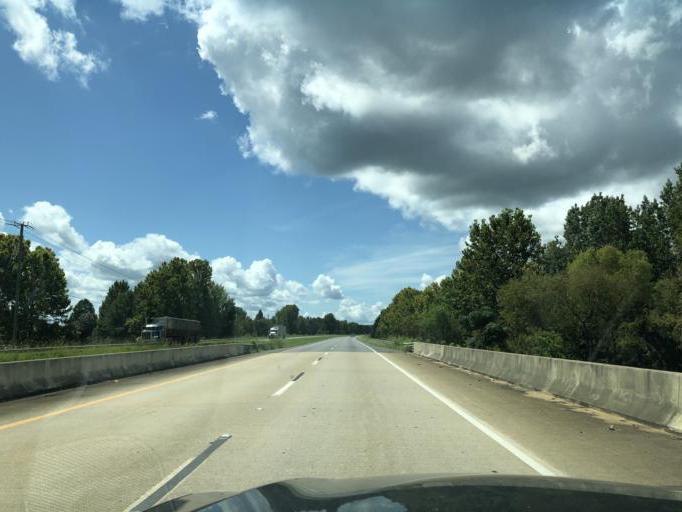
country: US
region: Alabama
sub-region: Barbour County
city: Eufaula
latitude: 31.9824
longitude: -85.1145
